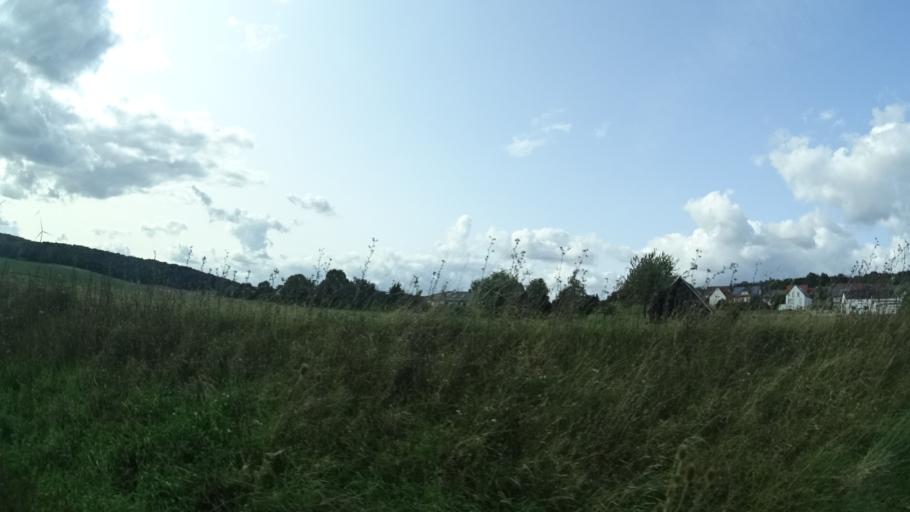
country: DE
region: Bavaria
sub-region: Regierungsbezirk Unterfranken
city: Greussenheim
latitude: 49.8118
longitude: 9.7547
